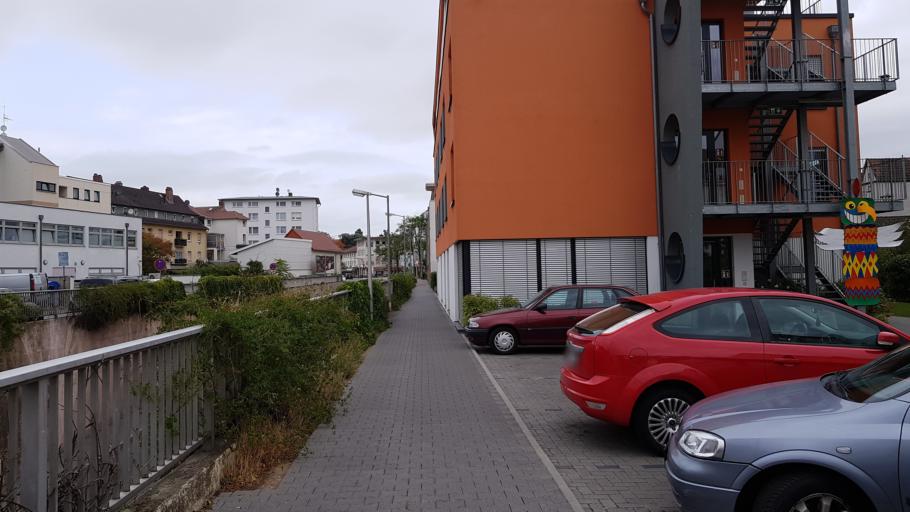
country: DE
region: Hesse
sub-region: Regierungsbezirk Darmstadt
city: Russelsheim
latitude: 49.9932
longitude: 8.4151
